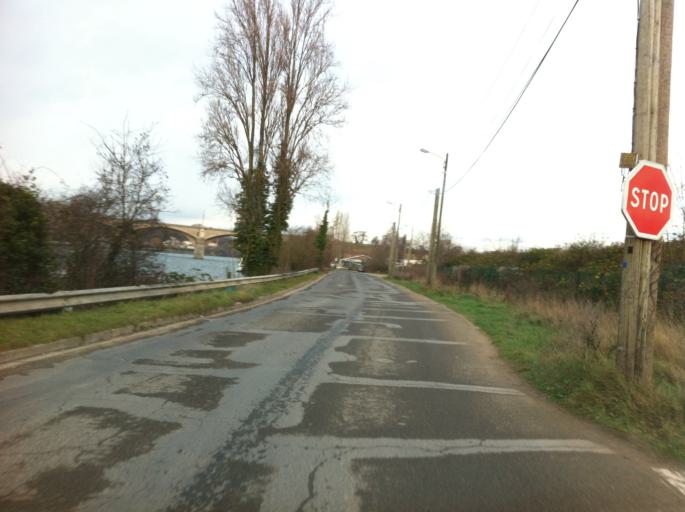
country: FR
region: Ile-de-France
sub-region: Departement de Seine-et-Marne
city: Le Mee-sur-Seine
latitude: 48.5284
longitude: 2.6362
